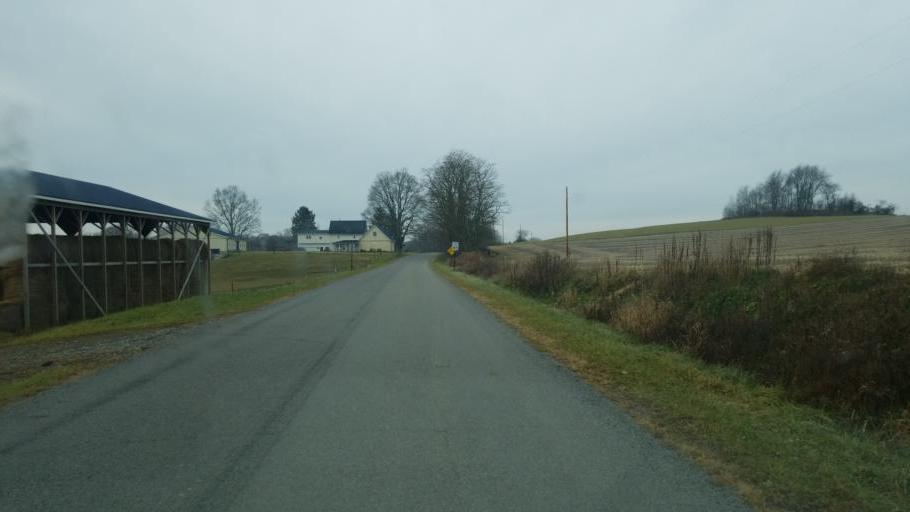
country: US
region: Pennsylvania
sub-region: Crawford County
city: Cochranton
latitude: 41.5074
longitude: -80.0882
